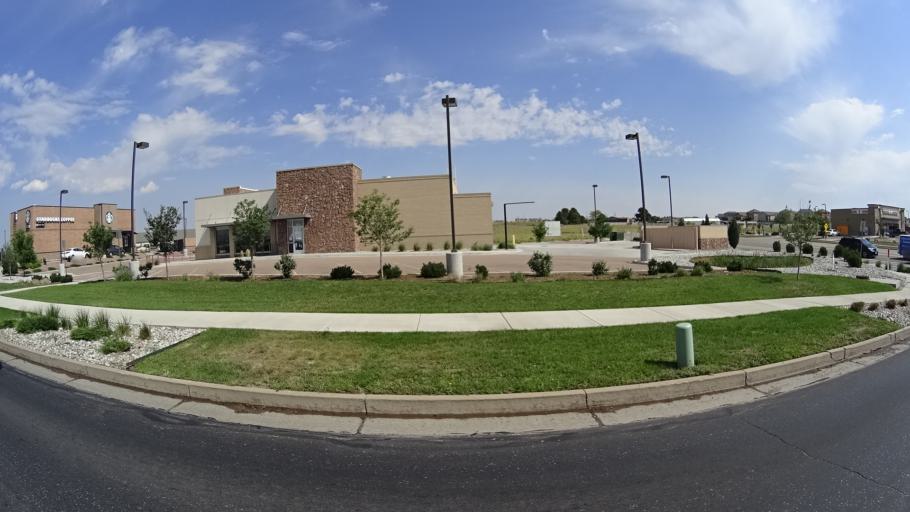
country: US
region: Colorado
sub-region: El Paso County
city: Cimarron Hills
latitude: 38.9259
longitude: -104.7155
